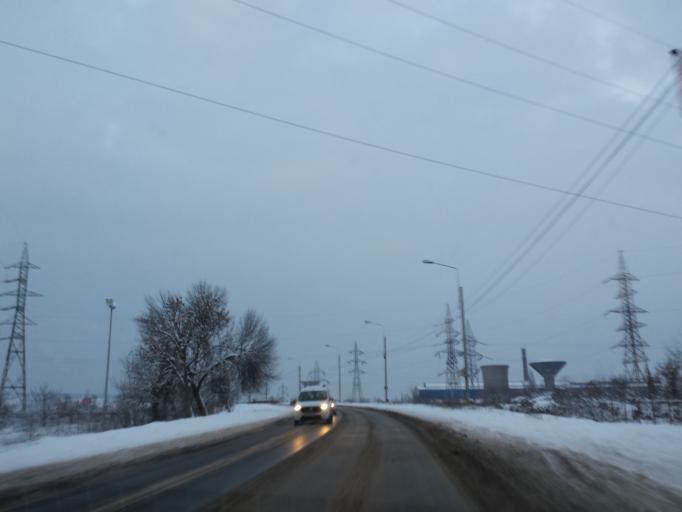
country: RO
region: Hunedoara
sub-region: Municipiul Hunedoara
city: Pestisu Mare
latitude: 45.7764
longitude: 22.9140
